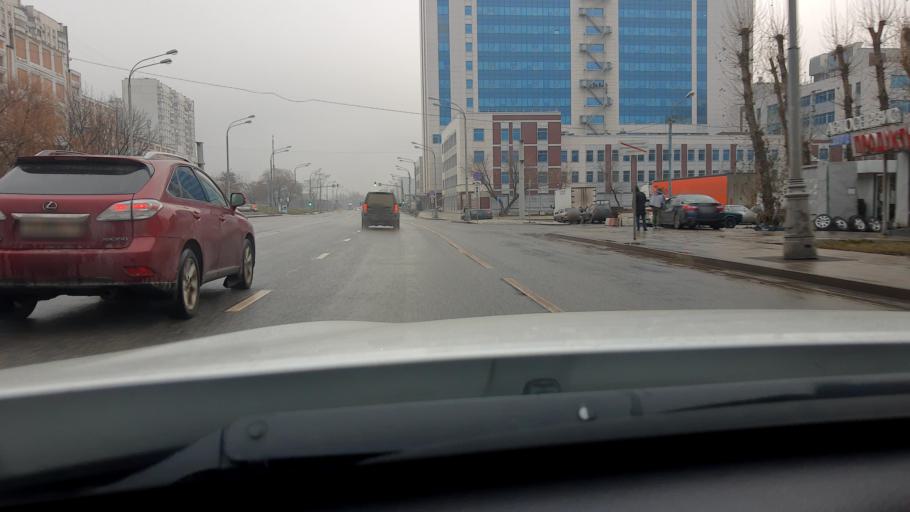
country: RU
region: Moskovskaya
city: Kozhukhovo
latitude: 55.7001
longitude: 37.6870
